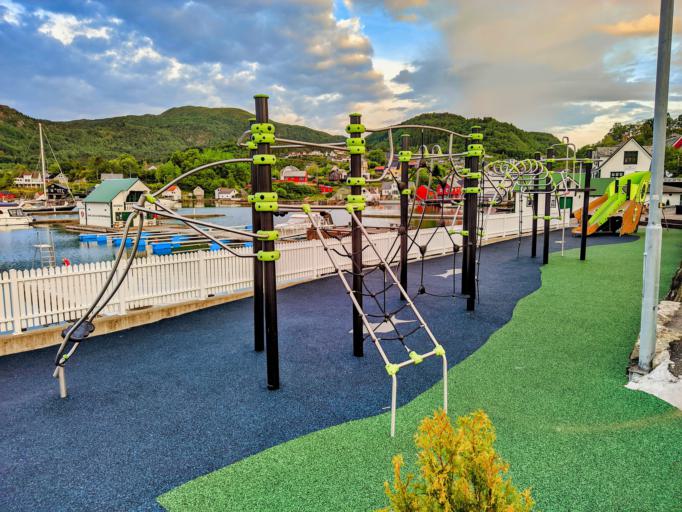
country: NO
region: Hordaland
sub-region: Tysnes
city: Uggdal
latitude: 60.0461
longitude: 5.5236
